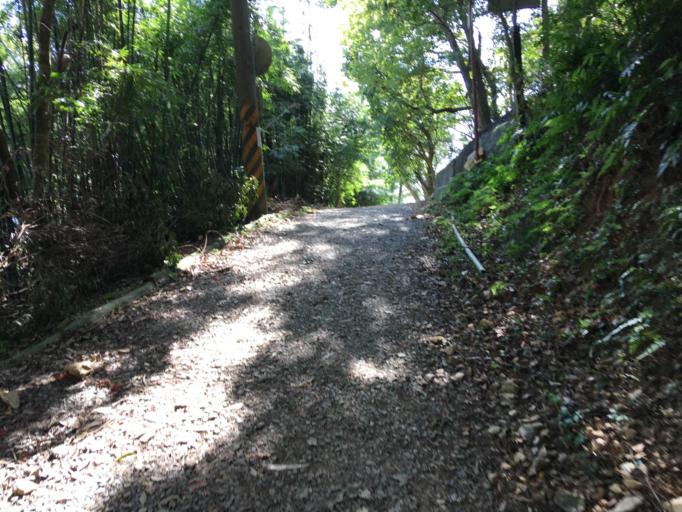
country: TW
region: Taiwan
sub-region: Yilan
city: Yilan
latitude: 24.8417
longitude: 121.7764
